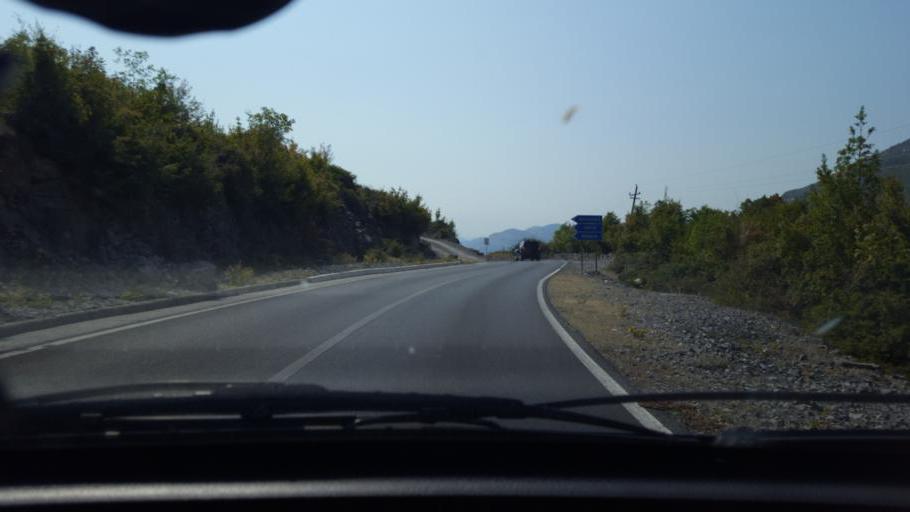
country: AL
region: Shkoder
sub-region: Rrethi i Malesia e Madhe
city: Kastrat
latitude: 42.3815
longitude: 19.4926
